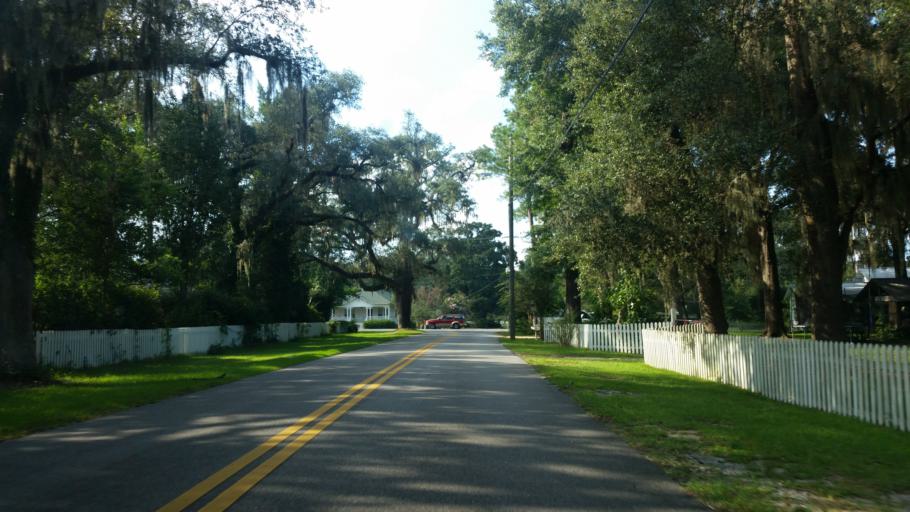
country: US
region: Florida
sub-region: Santa Rosa County
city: Bagdad
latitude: 30.6032
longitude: -87.0351
